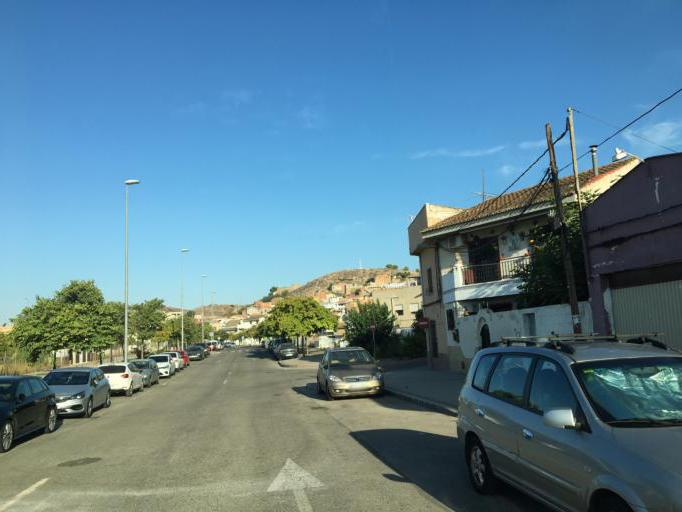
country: ES
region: Murcia
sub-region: Murcia
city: Murcia
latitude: 38.0162
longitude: -1.1454
